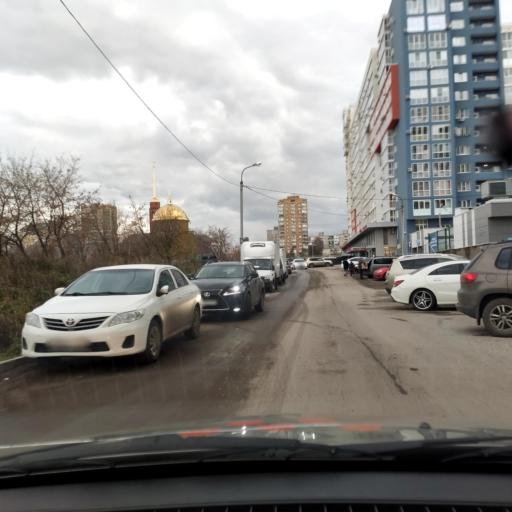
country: RU
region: Bashkortostan
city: Ufa
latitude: 54.7631
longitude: 56.0306
